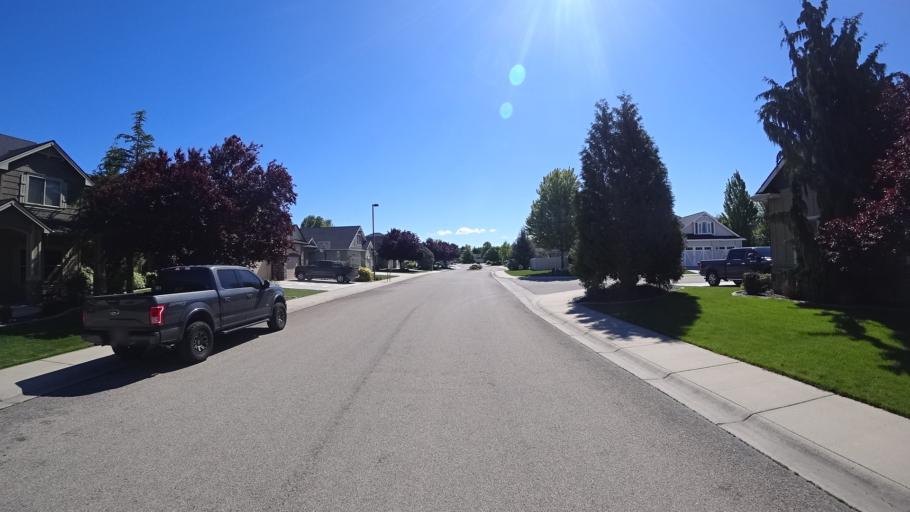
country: US
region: Idaho
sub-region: Ada County
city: Meridian
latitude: 43.6425
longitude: -116.3877
